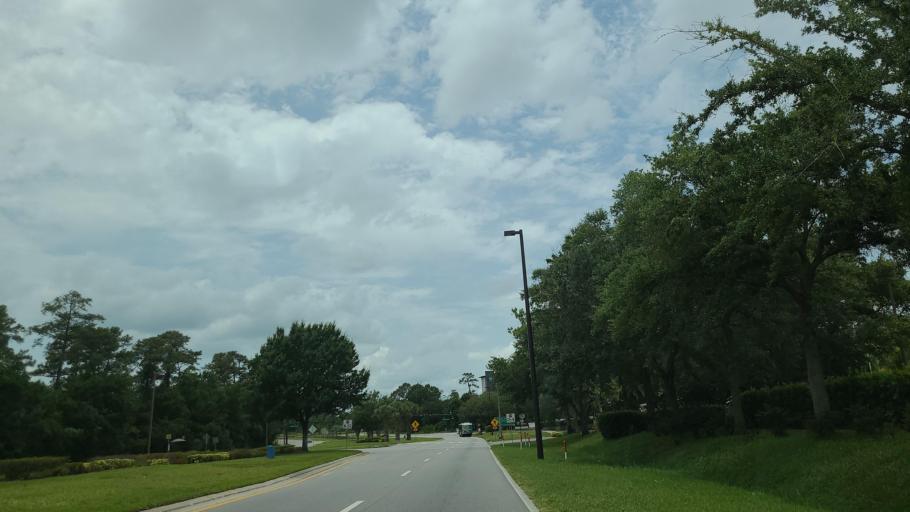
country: US
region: Florida
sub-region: Orange County
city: Williamsburg
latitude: 28.4189
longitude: -81.4650
